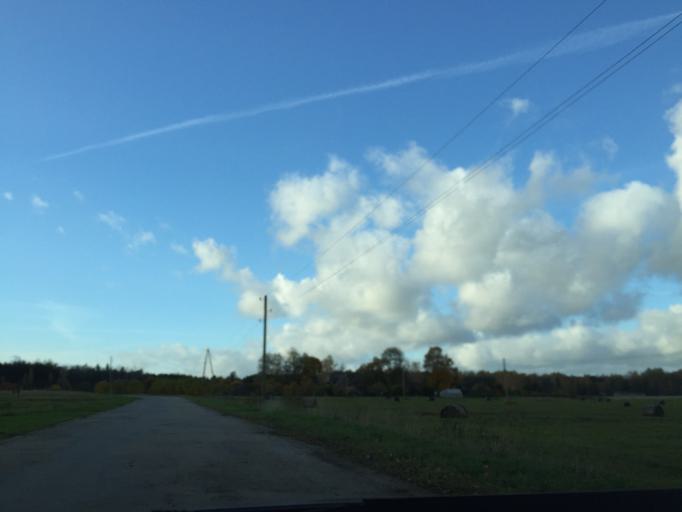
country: LV
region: Ogre
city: Jumprava
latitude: 56.7656
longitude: 25.0189
